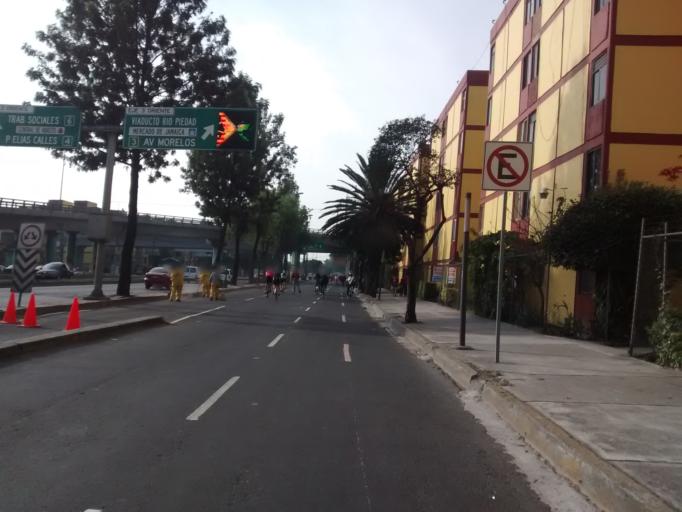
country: MX
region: Mexico City
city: Mexico City
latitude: 19.4149
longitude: -99.1128
